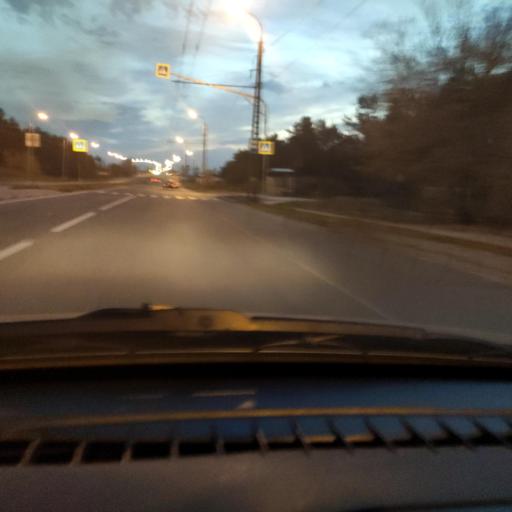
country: RU
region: Samara
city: Zhigulevsk
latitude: 53.5229
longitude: 49.5426
